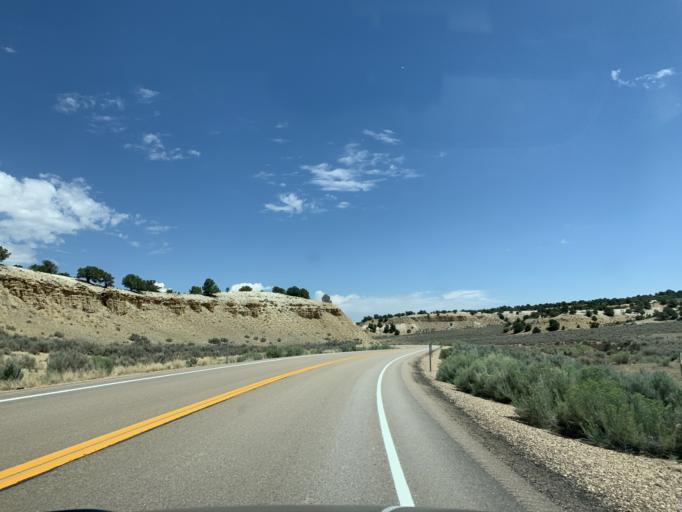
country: US
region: Utah
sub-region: Duchesne County
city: Duchesne
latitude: 39.9235
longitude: -110.2256
